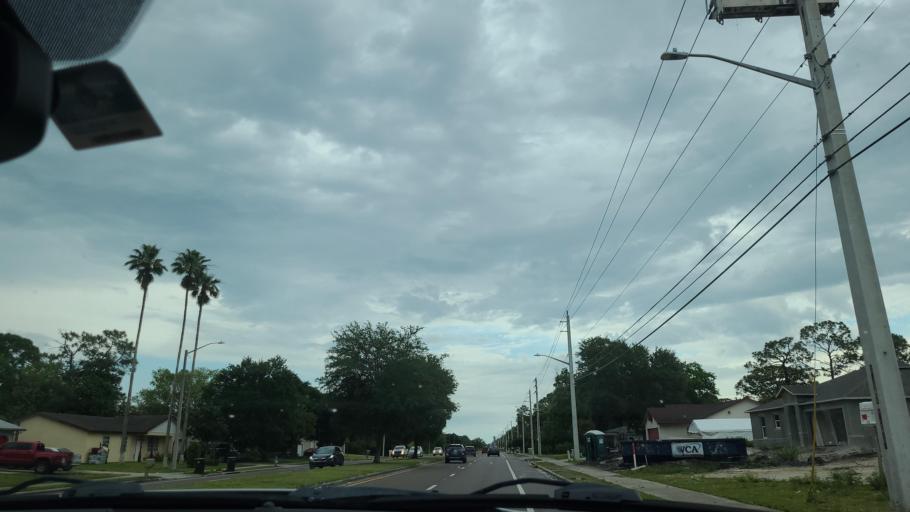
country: US
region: Florida
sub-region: Brevard County
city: June Park
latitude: 28.0319
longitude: -80.6901
